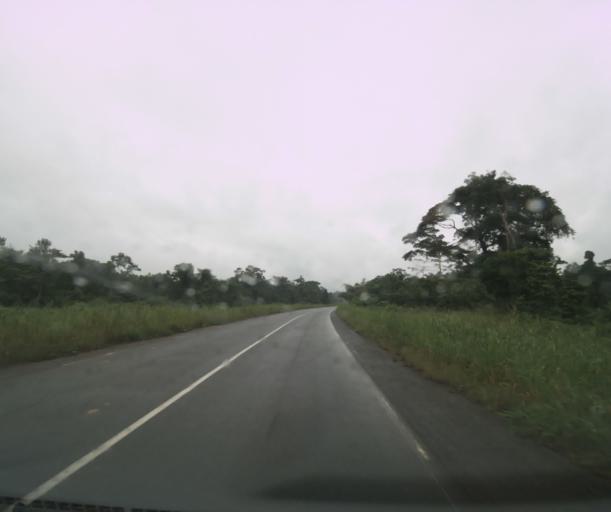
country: CM
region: Littoral
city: Edea
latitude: 3.4691
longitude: 10.1333
